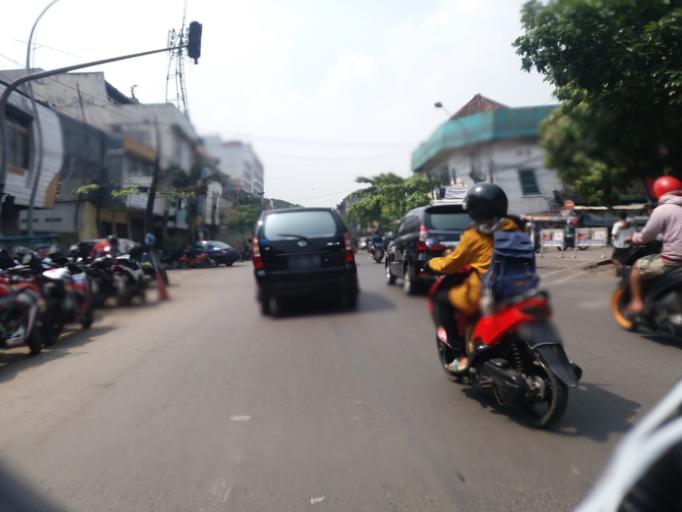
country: ID
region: West Java
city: Bandung
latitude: -6.9165
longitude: 107.5931
